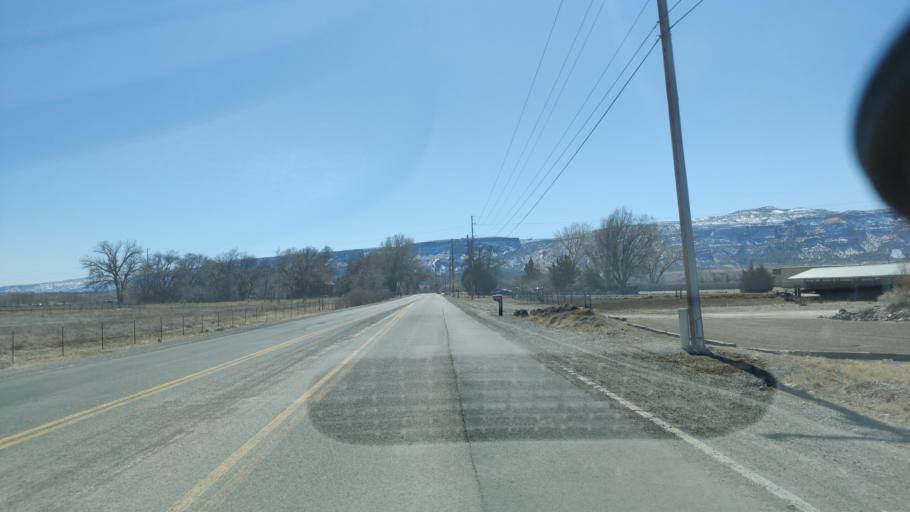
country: US
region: Colorado
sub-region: Mesa County
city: Fruita
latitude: 39.1417
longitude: -108.7012
